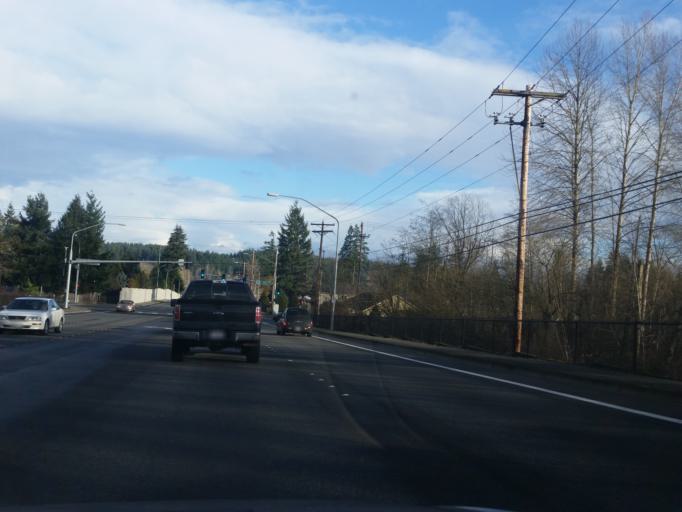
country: US
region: Washington
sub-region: Snohomish County
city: Martha Lake
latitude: 47.8094
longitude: -122.2221
